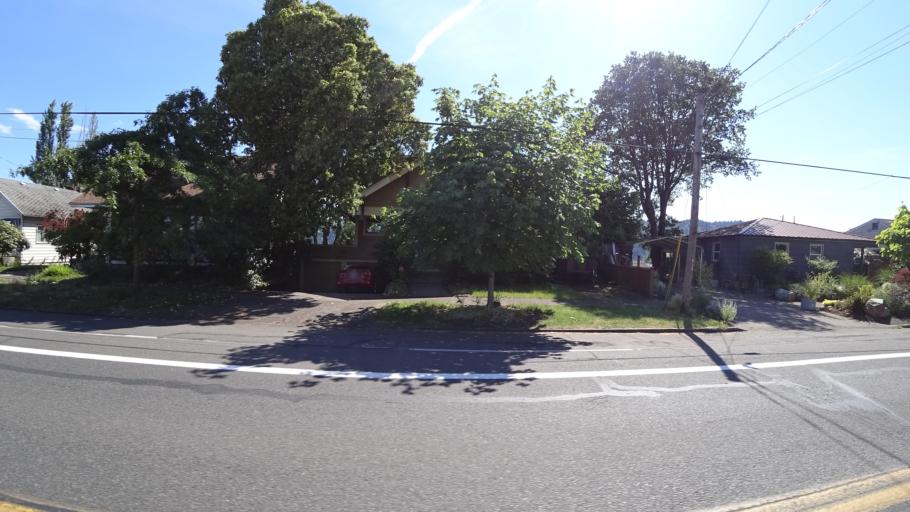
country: US
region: Oregon
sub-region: Washington County
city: West Haven
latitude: 45.5806
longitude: -122.7388
